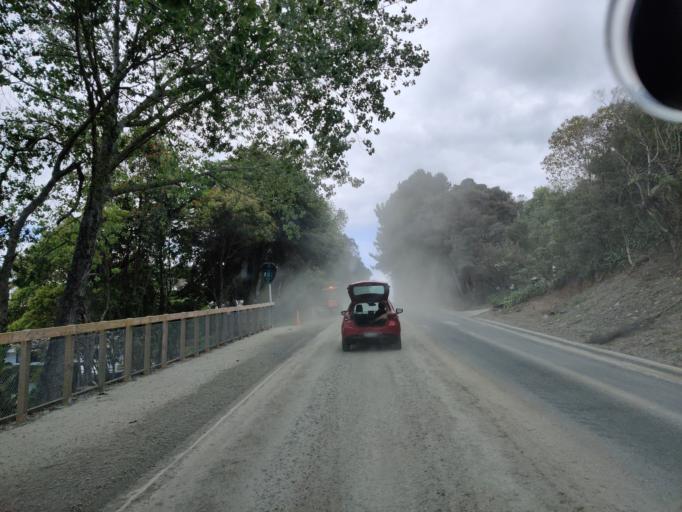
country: NZ
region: Northland
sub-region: Far North District
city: Taipa
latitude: -34.9929
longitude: 173.4755
